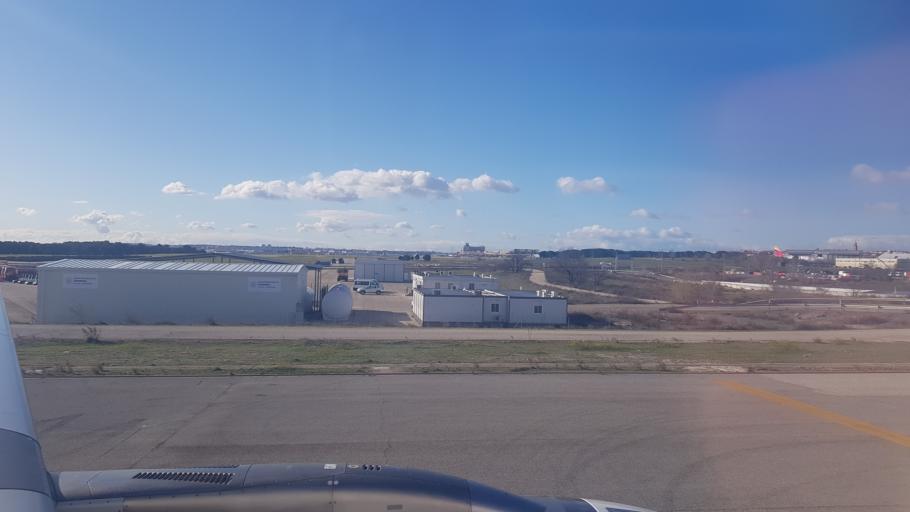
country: ES
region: Madrid
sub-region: Provincia de Madrid
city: Barajas de Madrid
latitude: 40.4875
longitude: -3.5648
